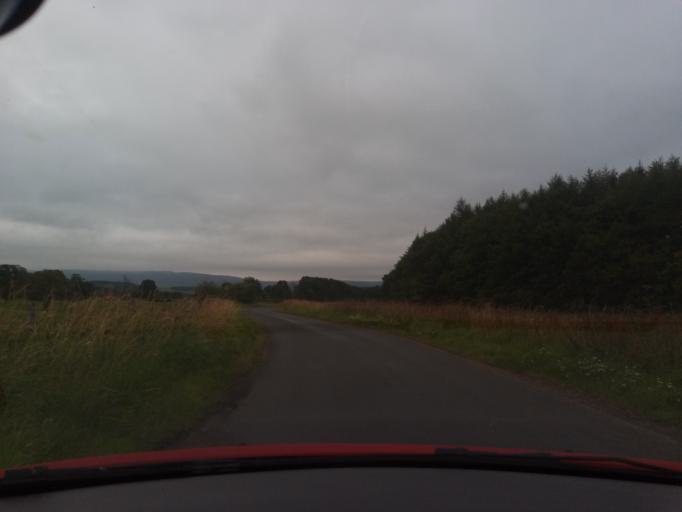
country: GB
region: England
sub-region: Northumberland
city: Otterburn
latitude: 55.3232
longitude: -2.0716
